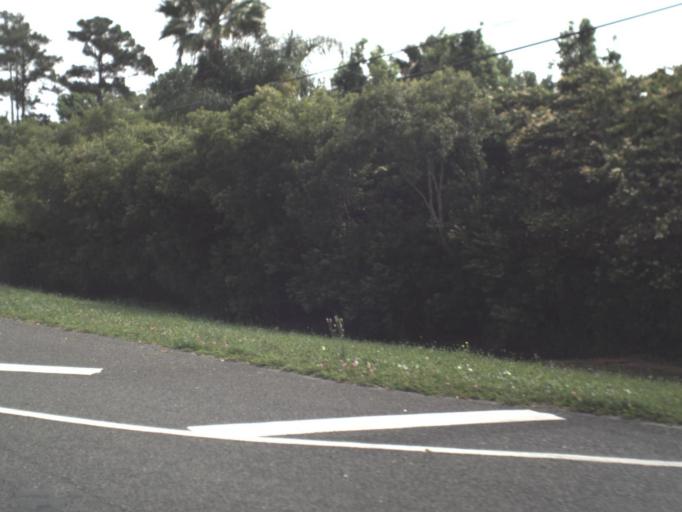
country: US
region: Florida
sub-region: Clay County
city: Orange Park
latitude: 30.1086
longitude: -81.7051
